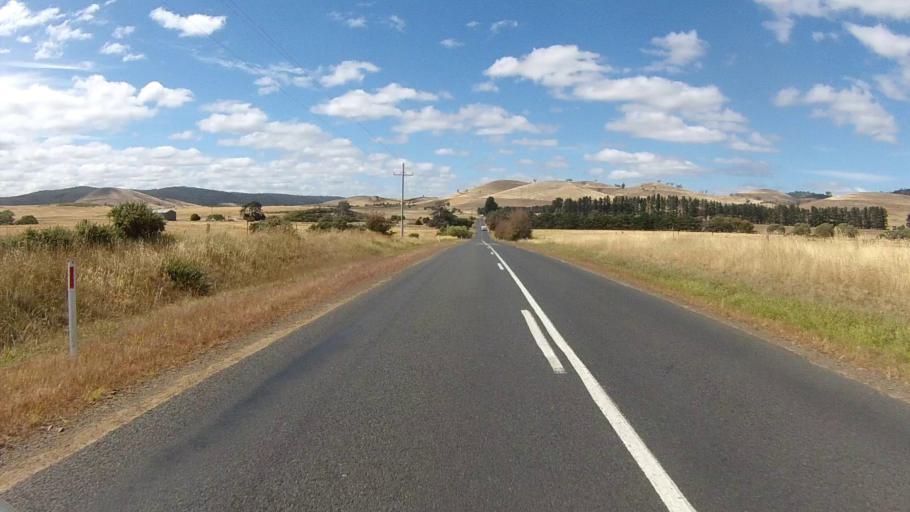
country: AU
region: Tasmania
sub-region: Brighton
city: Bridgewater
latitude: -42.5437
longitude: 147.3726
